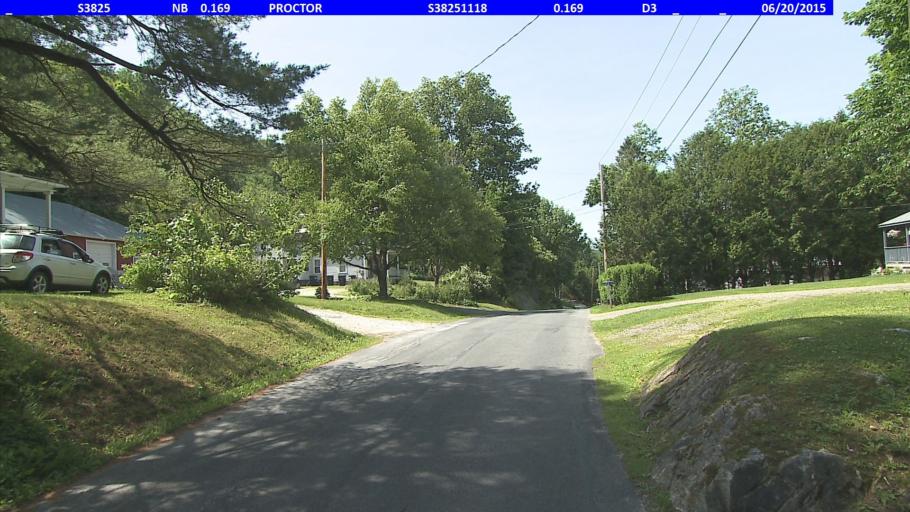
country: US
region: Vermont
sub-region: Rutland County
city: West Rutland
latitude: 43.6622
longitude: -73.0452
